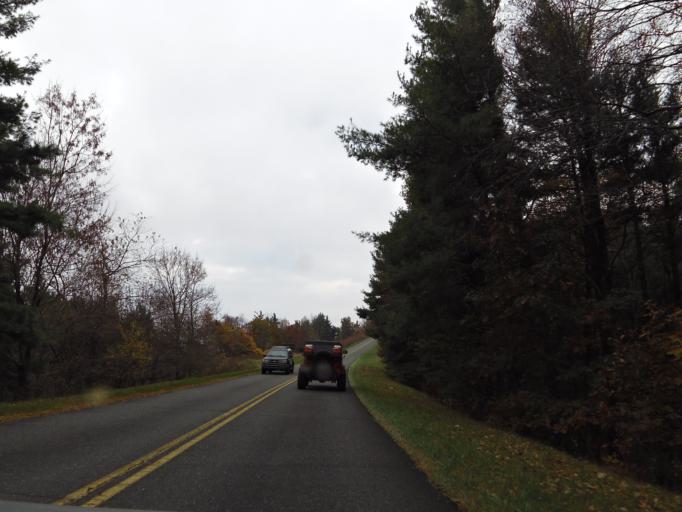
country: US
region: North Carolina
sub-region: Ashe County
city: West Jefferson
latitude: 36.2364
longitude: -81.4843
